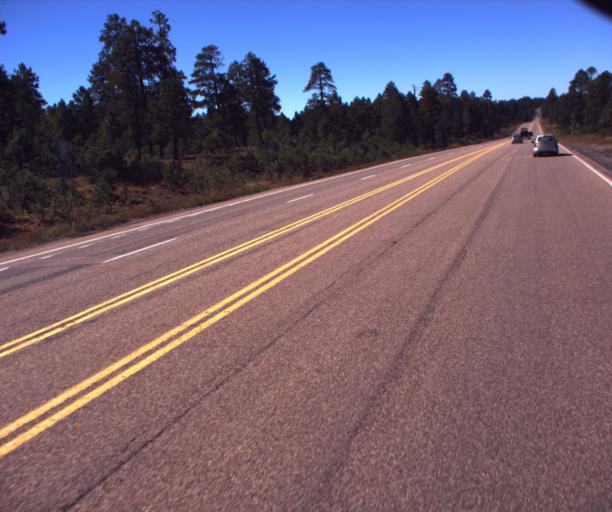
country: US
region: Arizona
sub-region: Navajo County
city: Heber-Overgaard
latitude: 34.3337
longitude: -110.7539
